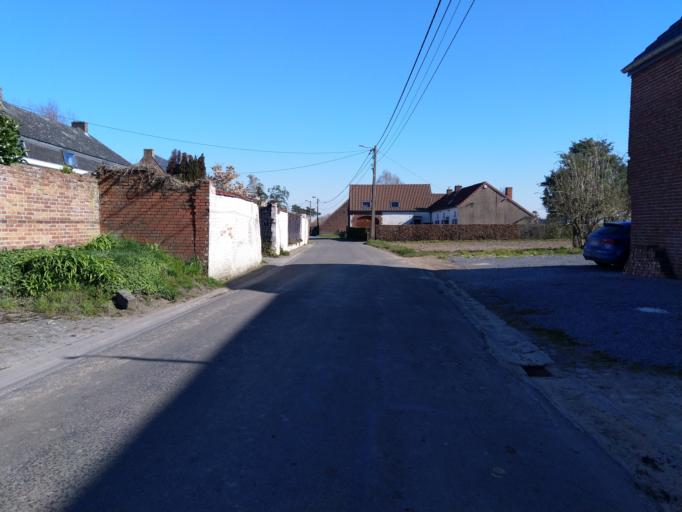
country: BE
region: Wallonia
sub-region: Province du Hainaut
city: Jurbise
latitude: 50.5161
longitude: 3.8523
